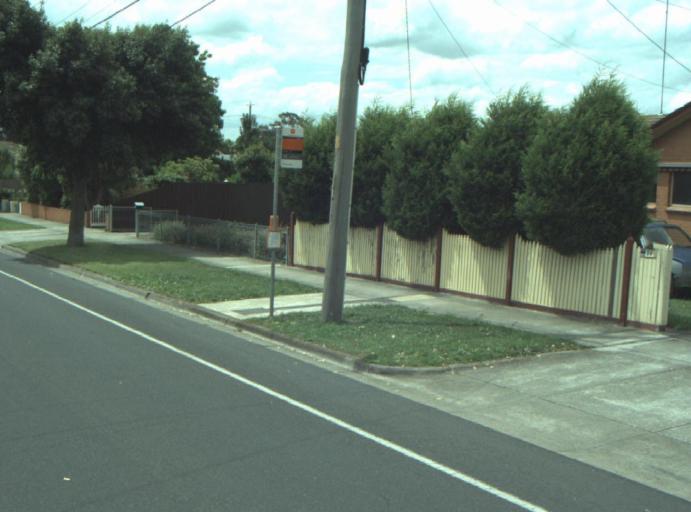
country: AU
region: Victoria
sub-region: Greater Geelong
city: Bell Park
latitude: -38.0688
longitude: 144.3671
